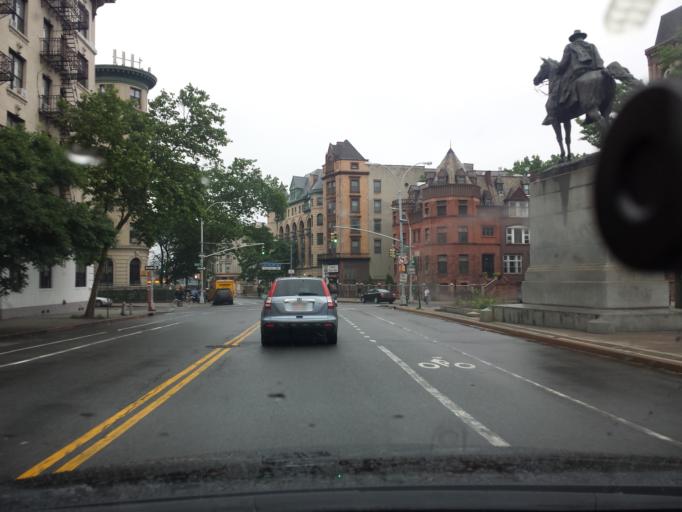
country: US
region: New York
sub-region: Kings County
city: Brooklyn
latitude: 40.6766
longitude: -73.9529
